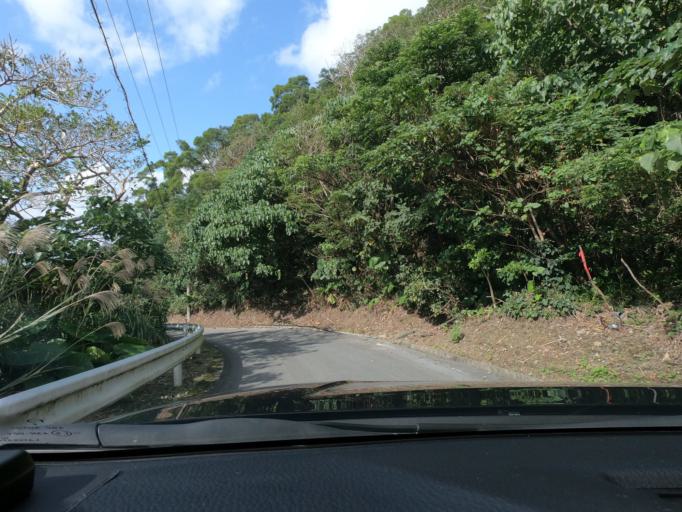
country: JP
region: Okinawa
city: Nago
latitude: 26.7569
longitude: 128.1943
